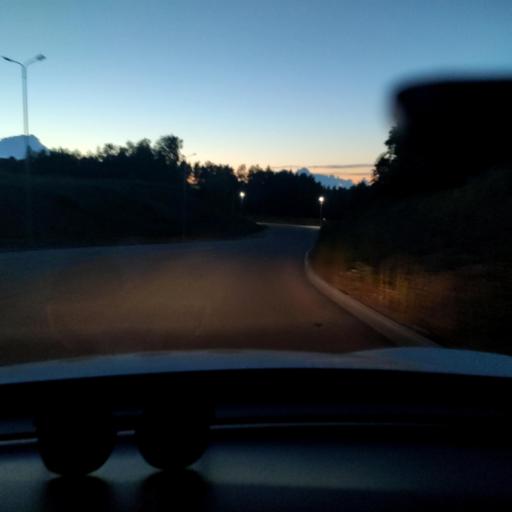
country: RU
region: Tatarstan
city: Osinovo
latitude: 55.8622
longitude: 48.9021
